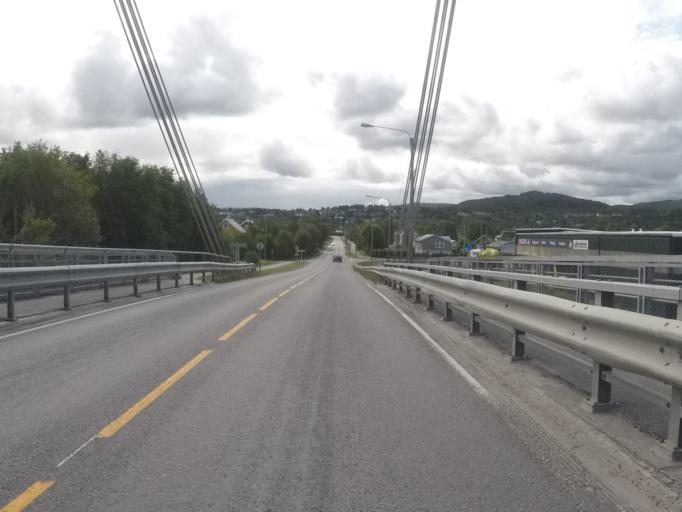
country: NO
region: Finnmark Fylke
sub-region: Alta
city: Alta
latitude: 69.9681
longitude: 23.3755
